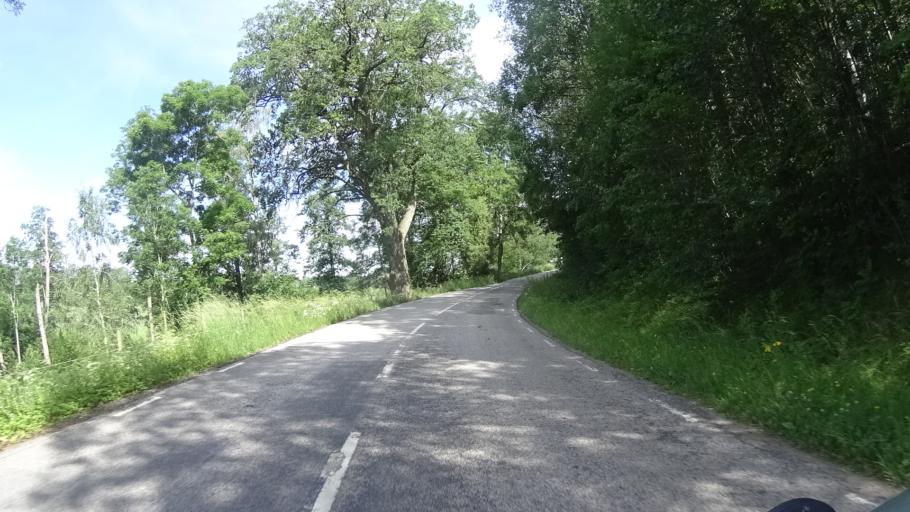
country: SE
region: Kalmar
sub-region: Vasterviks Kommun
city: Overum
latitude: 57.8998
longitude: 16.1729
